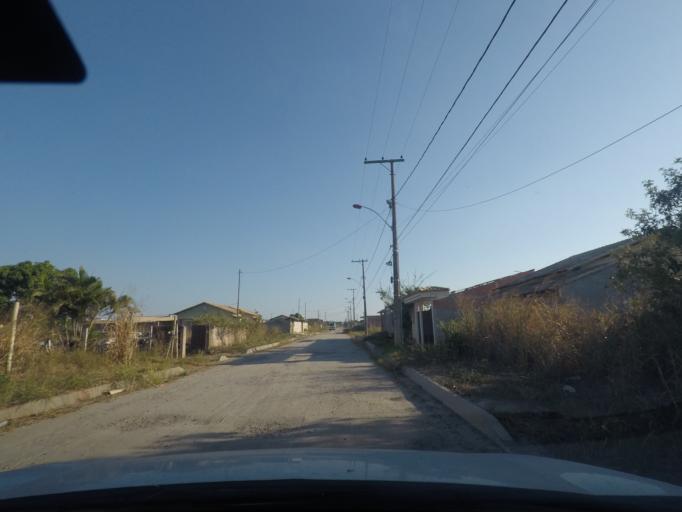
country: BR
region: Rio de Janeiro
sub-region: Marica
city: Marica
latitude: -22.9601
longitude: -42.9361
